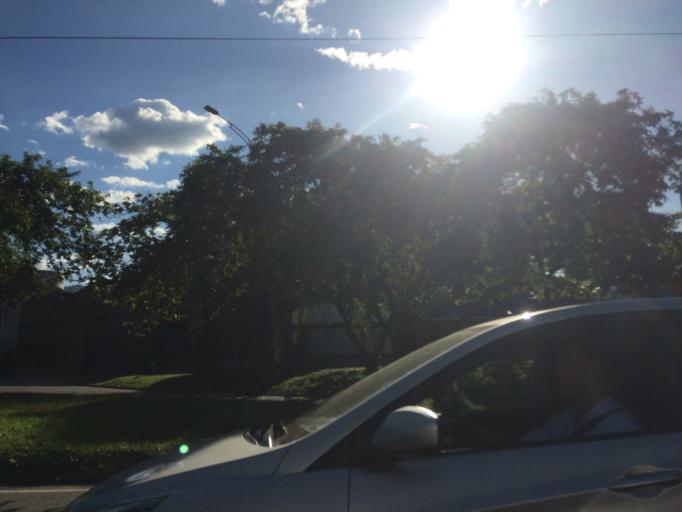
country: CO
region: Antioquia
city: Itagui
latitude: 6.2150
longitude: -75.5782
